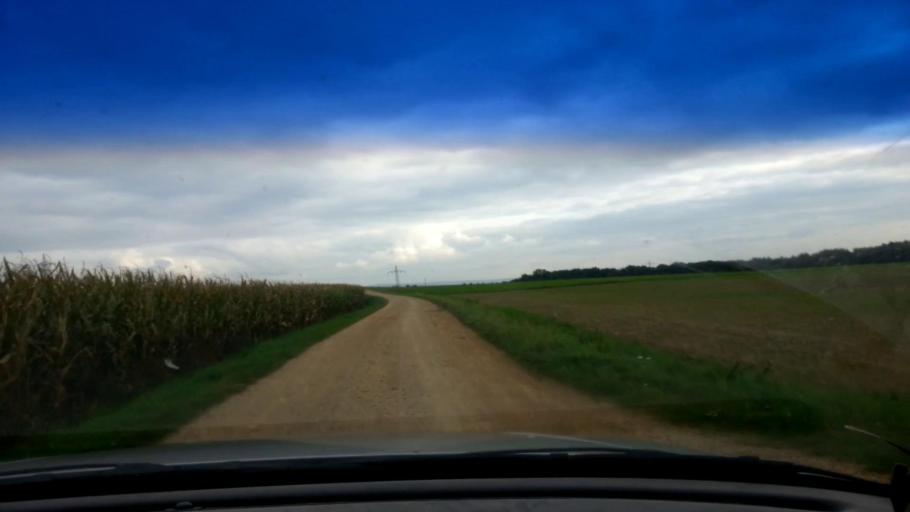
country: DE
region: Bavaria
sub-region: Upper Franconia
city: Zapfendorf
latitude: 49.9962
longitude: 10.9318
